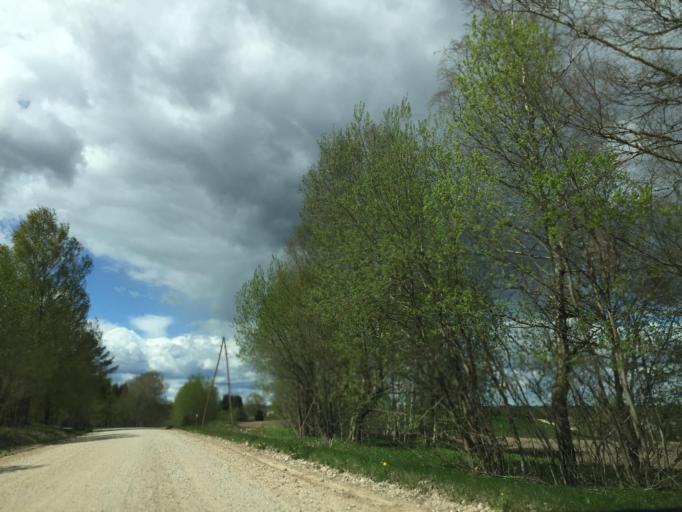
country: LV
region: Madonas Rajons
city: Madona
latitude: 56.9240
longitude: 26.0415
